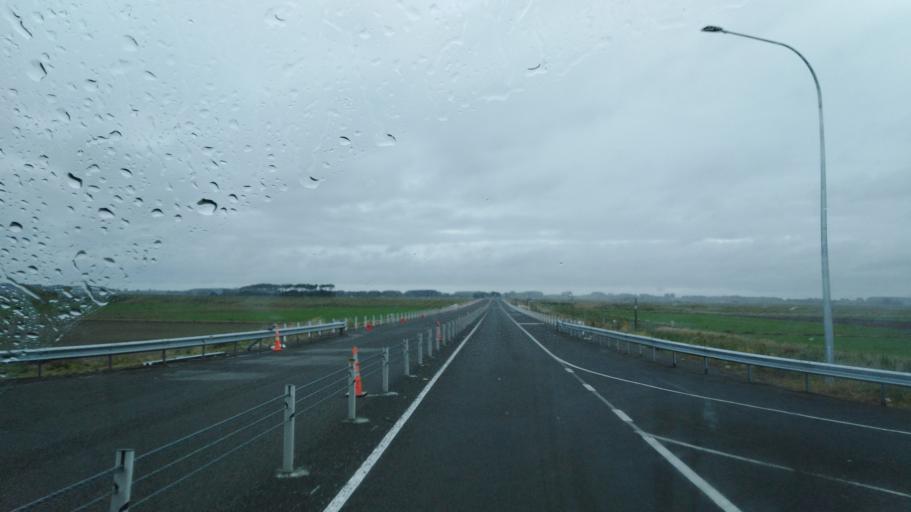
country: NZ
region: Manawatu-Wanganui
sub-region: Horowhenua District
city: Foxton
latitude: -40.5122
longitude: 175.2782
